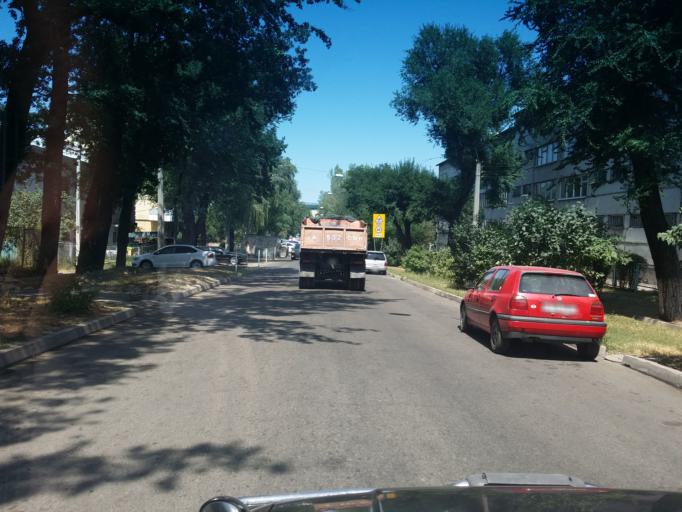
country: KZ
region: Almaty Qalasy
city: Almaty
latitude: 43.2597
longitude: 76.9304
